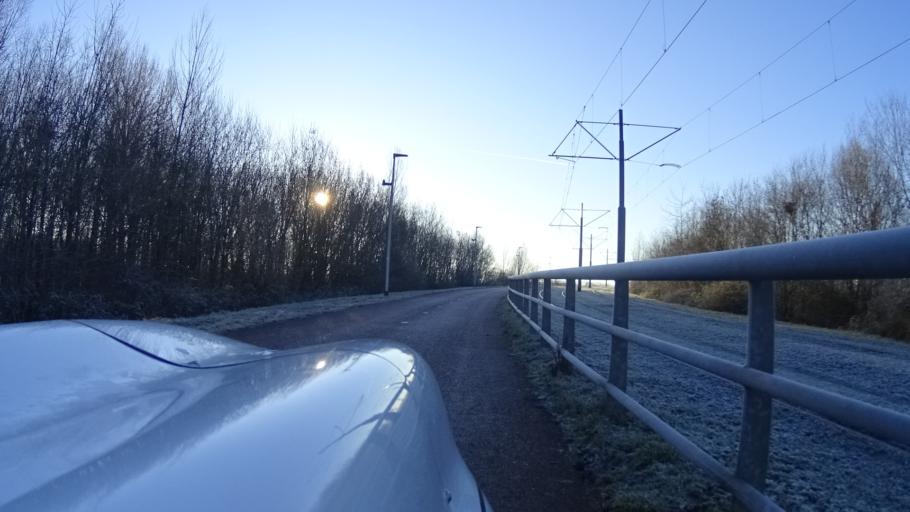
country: NL
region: South Holland
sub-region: Gemeente Barendrecht
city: Barendrecht
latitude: 51.8680
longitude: 4.5026
